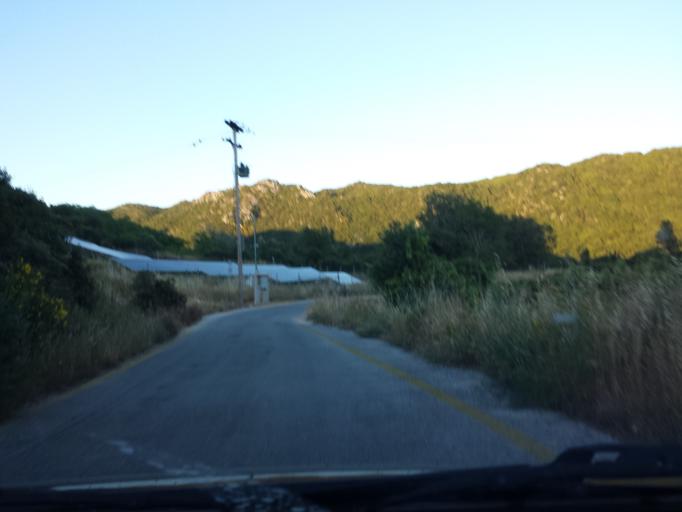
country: GR
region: Ionian Islands
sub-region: Nomos Kerkyras
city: Acharavi
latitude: 39.7404
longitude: 19.8369
